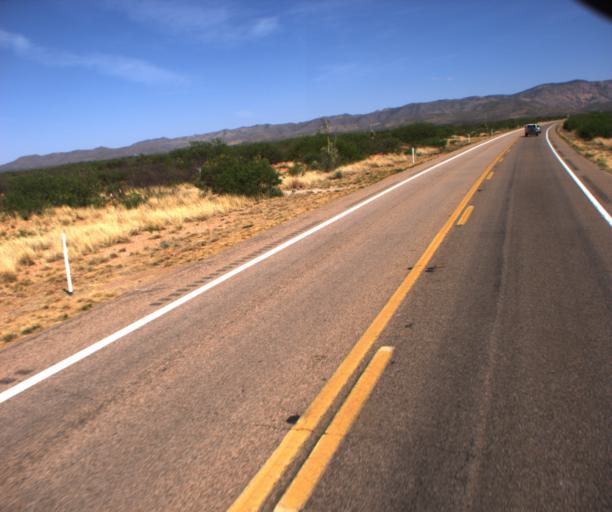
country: US
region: Arizona
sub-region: Cochise County
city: Sierra Vista Southeast
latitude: 31.5405
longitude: -110.0739
